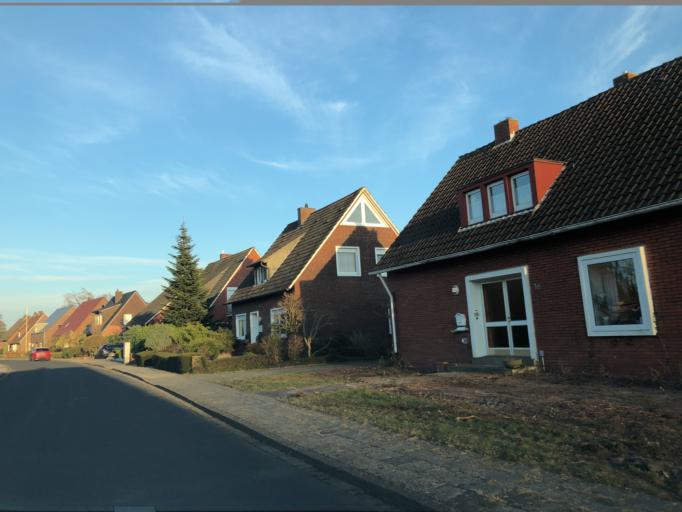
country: DE
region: Lower Saxony
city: Papenburg
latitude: 53.0791
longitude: 7.3837
